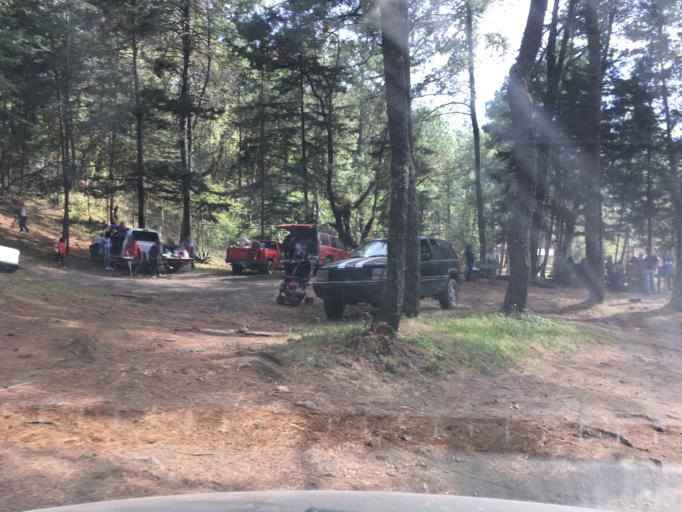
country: MX
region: Michoacan
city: Angahuan
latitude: 19.5415
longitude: -102.2334
